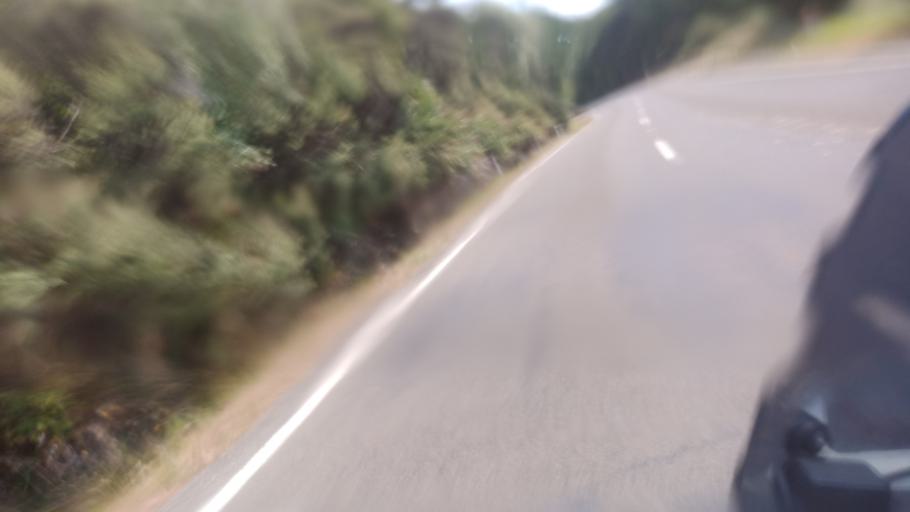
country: NZ
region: Bay of Plenty
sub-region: Opotiki District
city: Opotiki
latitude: -37.5729
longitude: 178.0583
